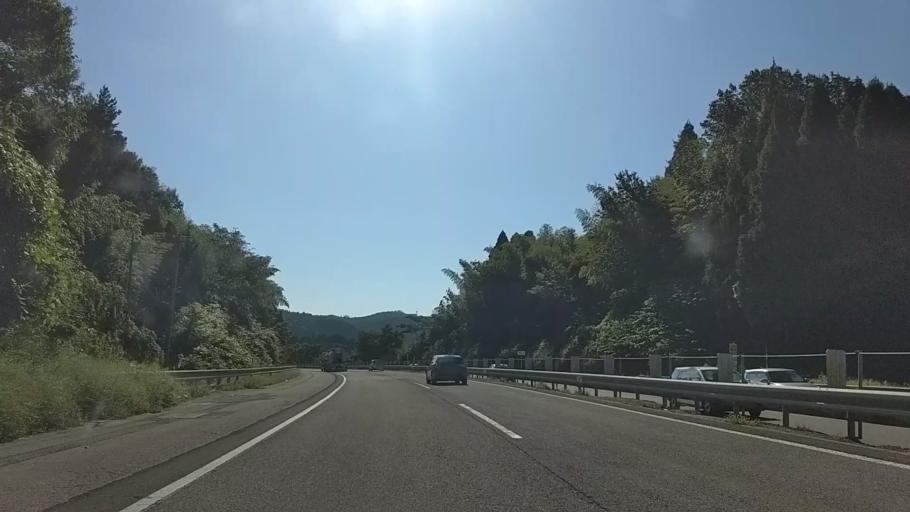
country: JP
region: Ishikawa
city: Tsubata
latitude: 36.5987
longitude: 136.7346
